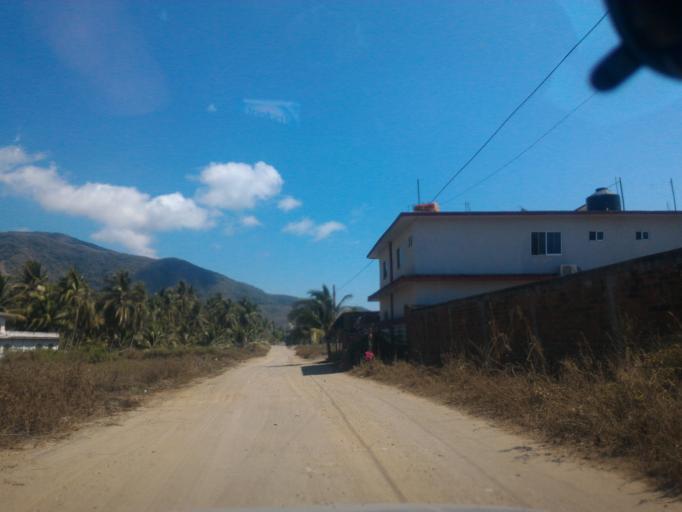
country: MX
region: Michoacan
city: Coahuayana Viejo
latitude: 18.5850
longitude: -103.6772
